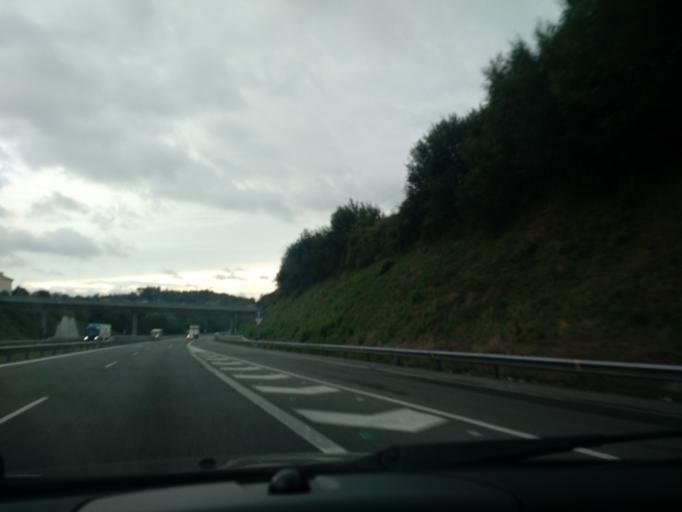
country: ES
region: Galicia
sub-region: Provincia da Coruna
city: Oleiros
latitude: 43.2956
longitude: -8.3045
